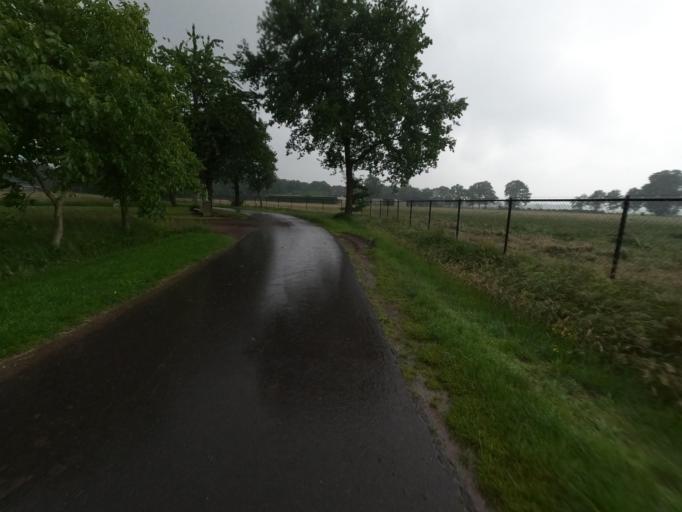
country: BE
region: Flanders
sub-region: Provincie Antwerpen
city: Kalmthout
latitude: 51.4102
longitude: 4.5144
